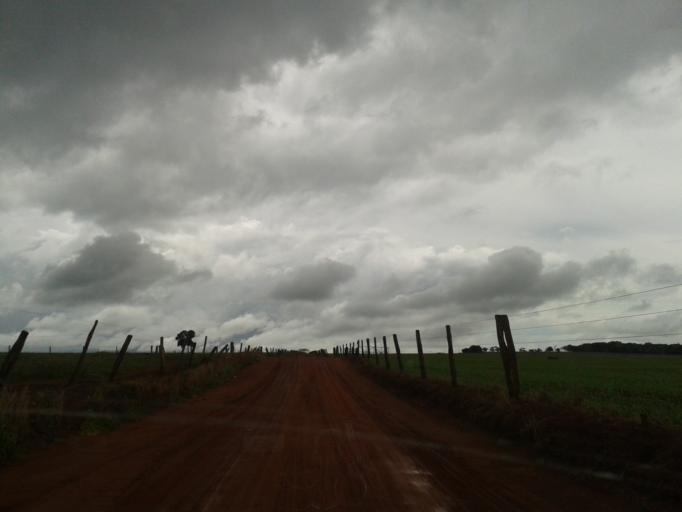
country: BR
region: Minas Gerais
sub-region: Santa Vitoria
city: Santa Vitoria
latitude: -18.6724
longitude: -49.9308
